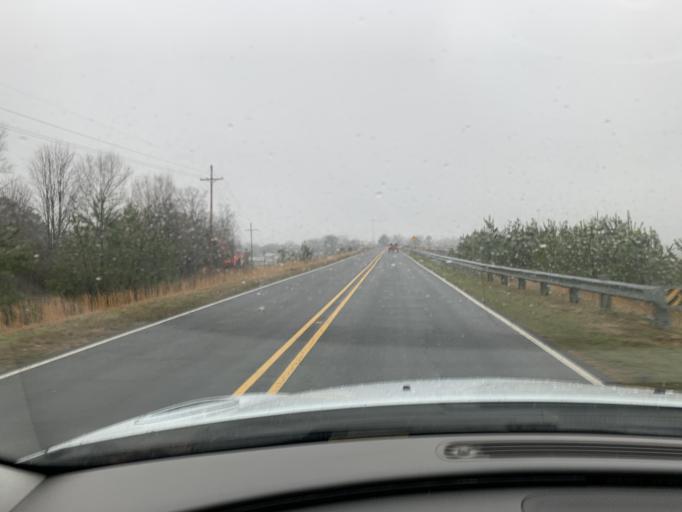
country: US
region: Mississippi
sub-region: De Soto County
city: Hernando
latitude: 34.8598
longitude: -89.9863
